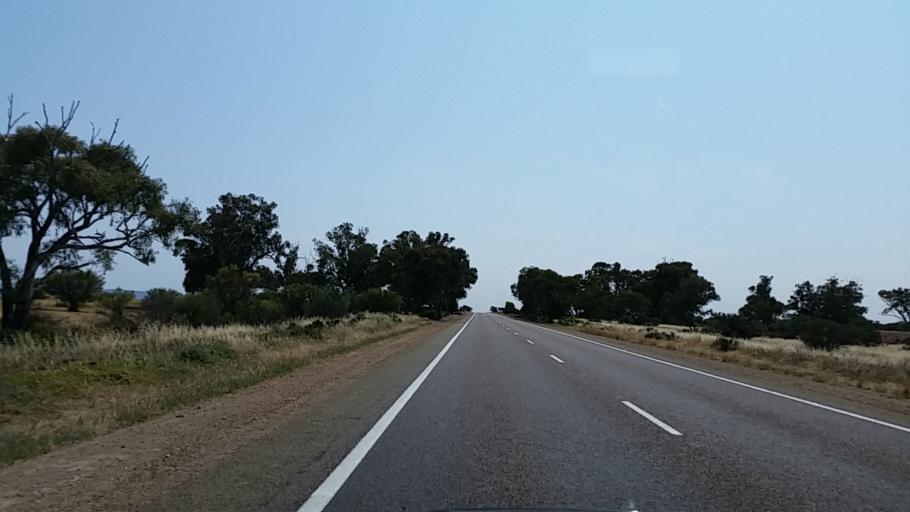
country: AU
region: South Australia
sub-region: Port Pirie City and Dists
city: Port Pirie
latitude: -32.8214
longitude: 137.9751
